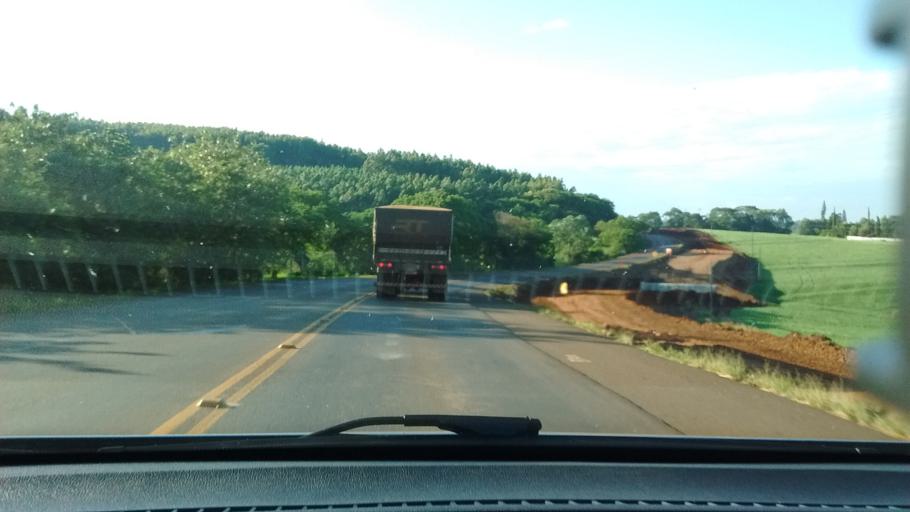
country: BR
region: Parana
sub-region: Cascavel
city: Cascavel
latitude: -25.2050
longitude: -53.5972
